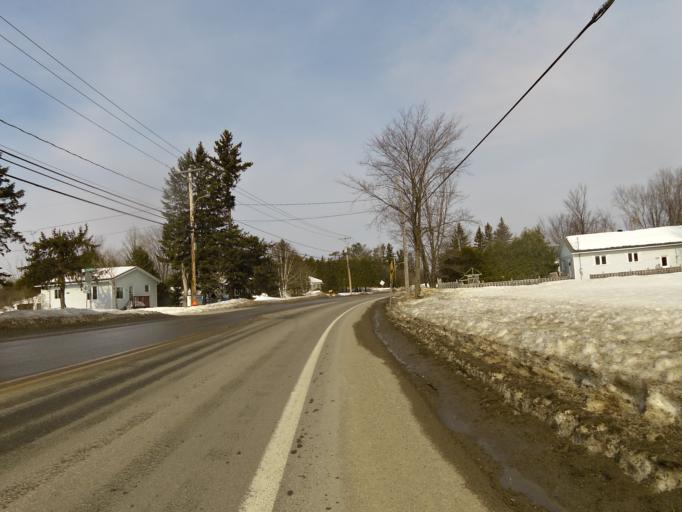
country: CA
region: Quebec
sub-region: Outaouais
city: Gatineau
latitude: 45.4970
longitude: -75.7788
